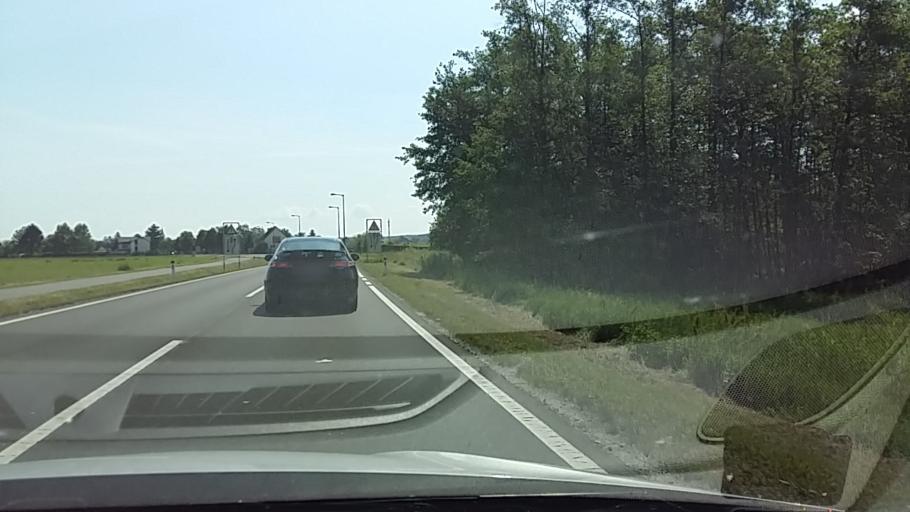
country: AT
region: Burgenland
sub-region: Politischer Bezirk Jennersdorf
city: Mogersdorf
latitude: 46.9469
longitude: 16.2160
